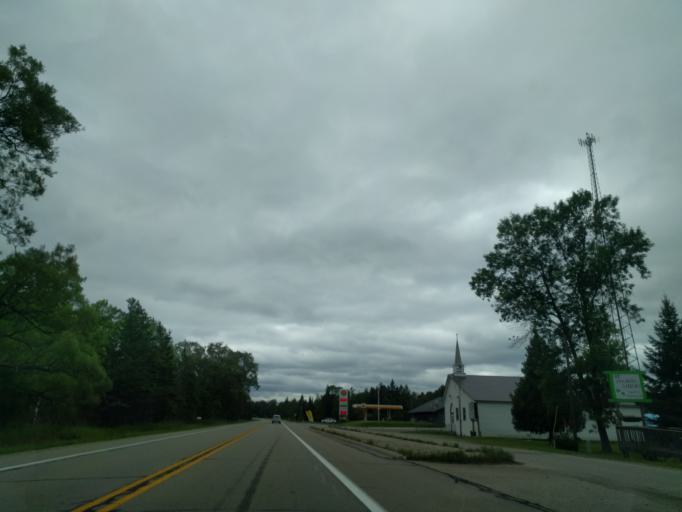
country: US
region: Michigan
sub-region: Menominee County
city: Menominee
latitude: 45.4105
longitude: -87.3556
